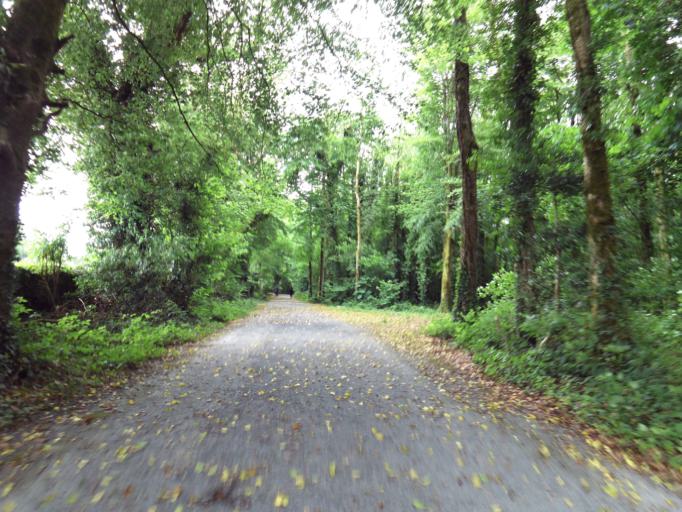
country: IE
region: Connaught
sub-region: County Galway
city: Gort
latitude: 53.0848
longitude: -8.8425
